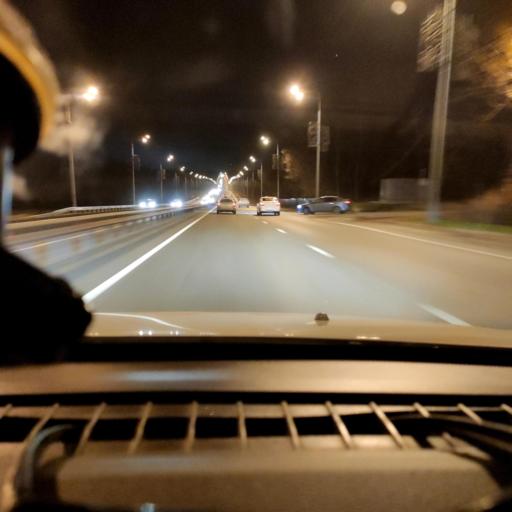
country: RU
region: Samara
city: Novosemeykino
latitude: 53.3410
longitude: 50.2327
